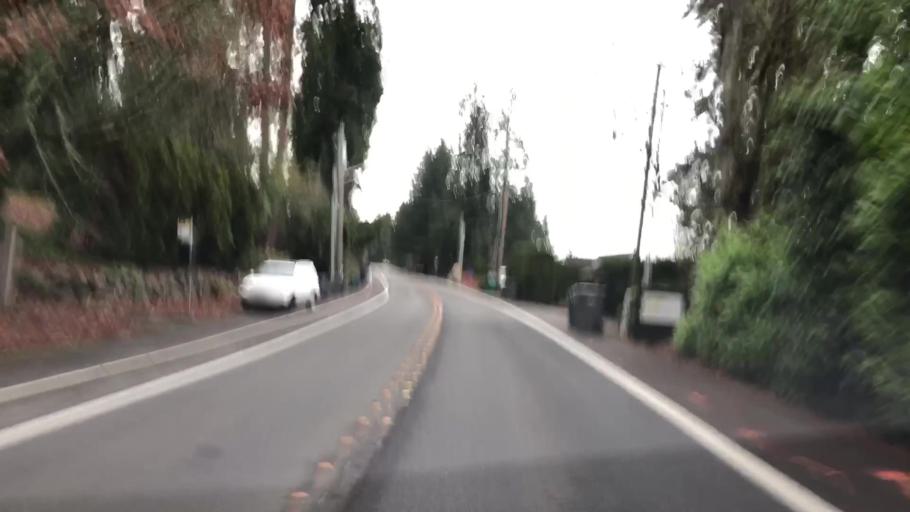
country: US
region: Washington
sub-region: King County
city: Sammamish
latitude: 47.6369
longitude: -122.0941
